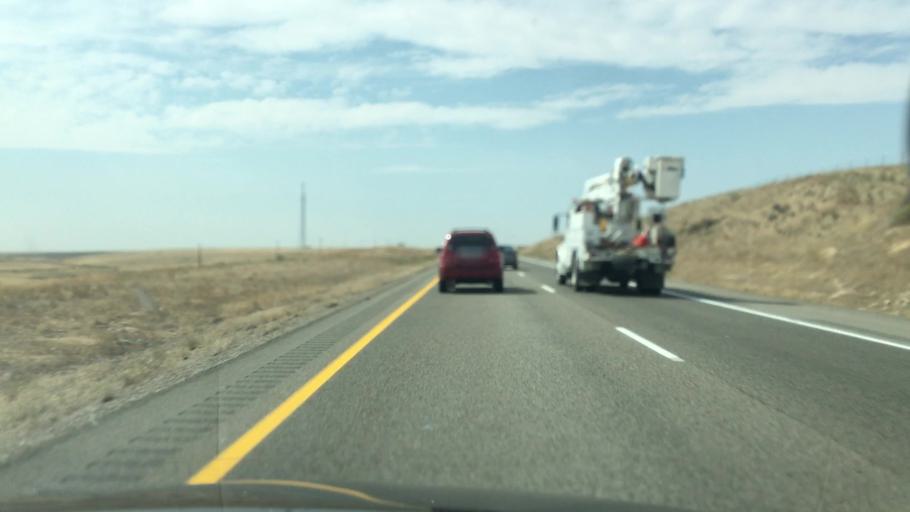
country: US
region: Idaho
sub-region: Ada County
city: Boise
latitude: 43.4451
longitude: -116.0722
